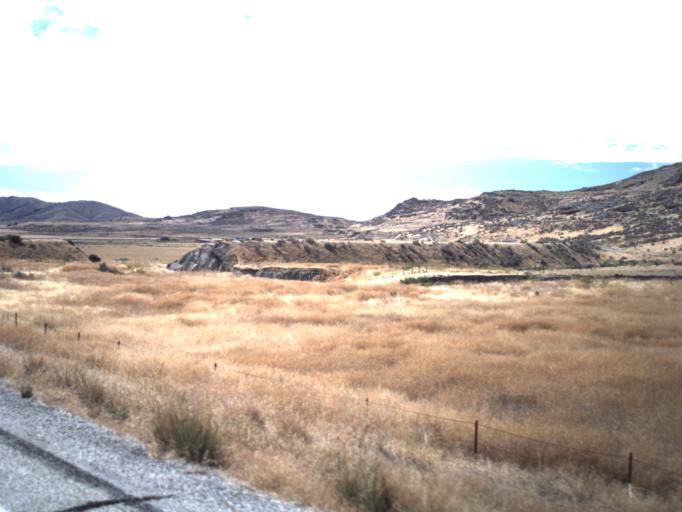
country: US
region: Utah
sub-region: Box Elder County
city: Tremonton
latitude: 41.6729
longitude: -112.4471
